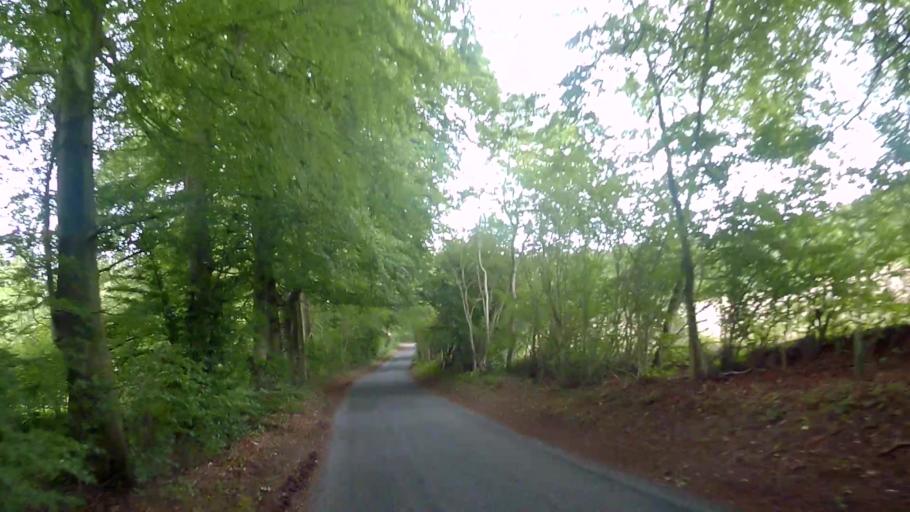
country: GB
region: England
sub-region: Hampshire
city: Overton
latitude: 51.1933
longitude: -1.2800
